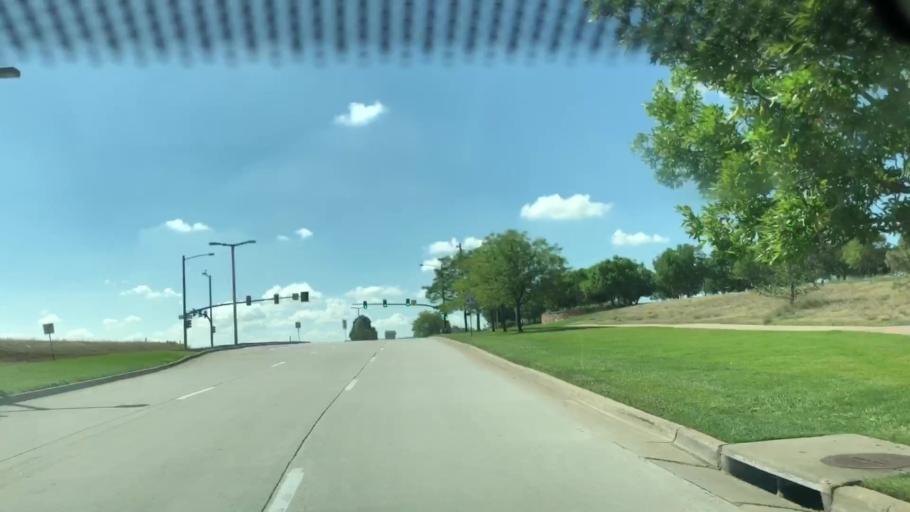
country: US
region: Colorado
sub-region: Douglas County
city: Meridian
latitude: 39.5502
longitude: -104.8396
